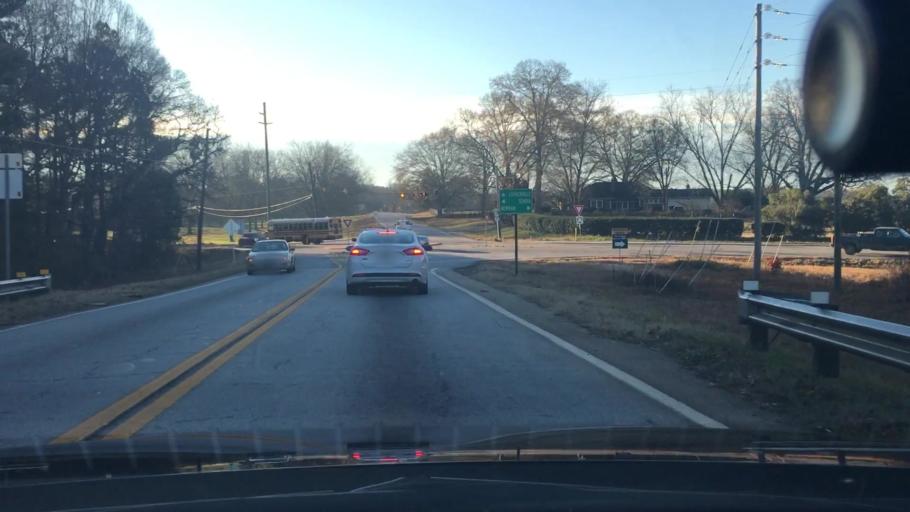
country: US
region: Georgia
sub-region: Fayette County
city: Peachtree City
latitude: 33.3305
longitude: -84.6452
